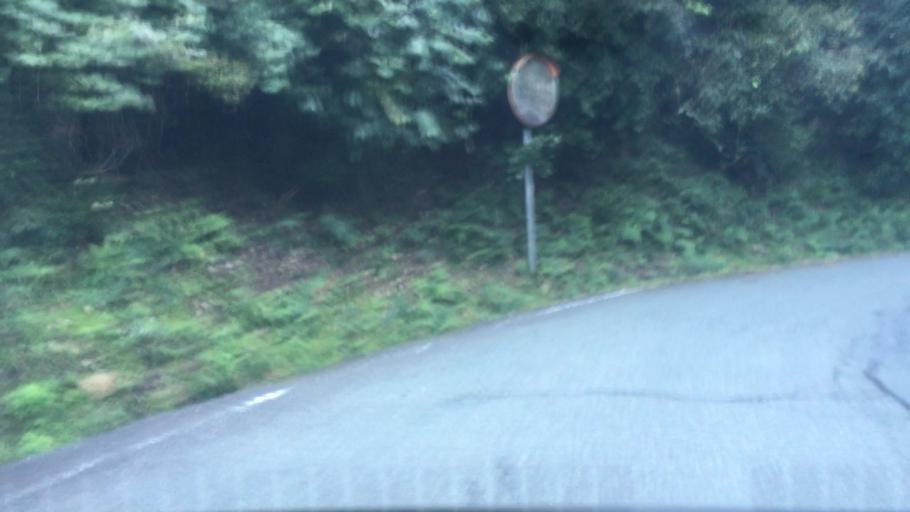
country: JP
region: Hyogo
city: Toyooka
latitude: 35.6101
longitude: 134.8377
